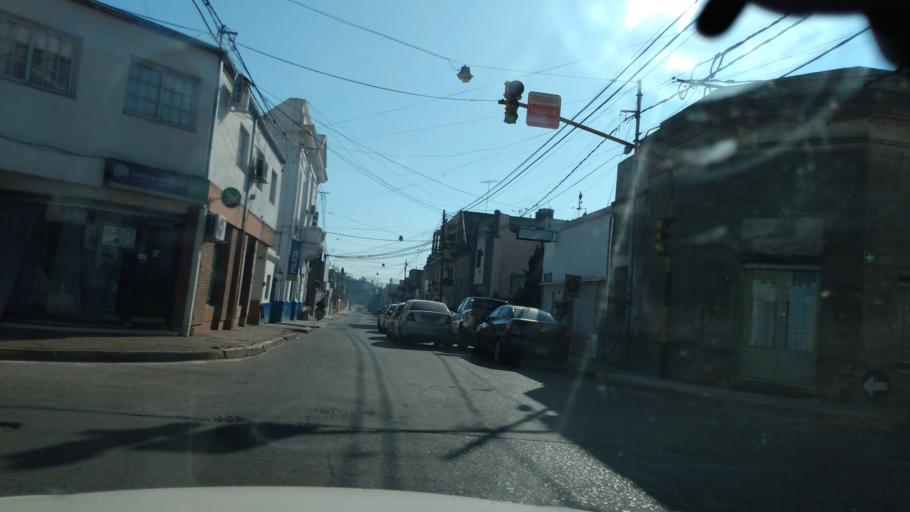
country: AR
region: Buenos Aires
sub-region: Partido de Lujan
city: Lujan
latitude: -34.5675
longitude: -59.1175
